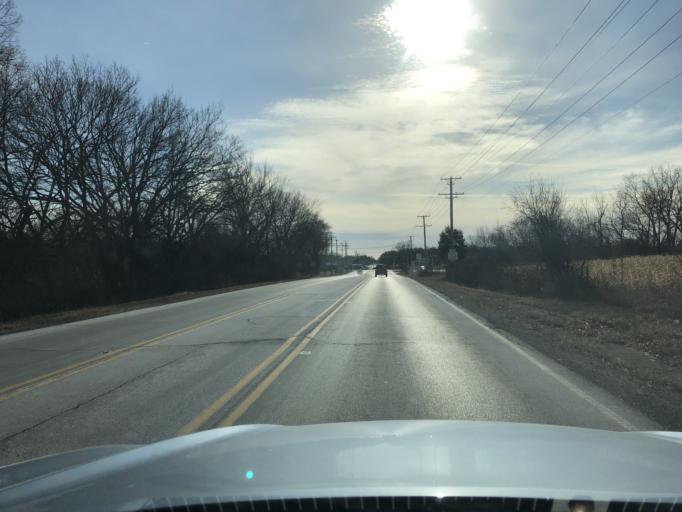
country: US
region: Illinois
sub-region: Lake County
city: Third Lake
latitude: 42.3888
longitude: -88.0041
